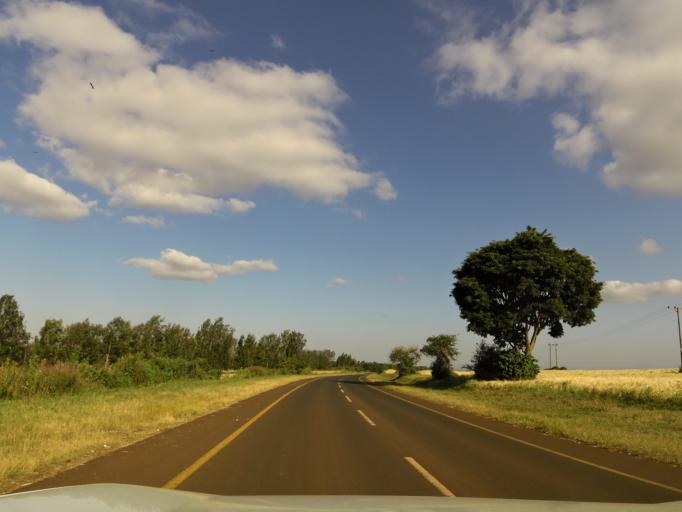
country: TZ
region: Arusha
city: Kiratu
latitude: -3.3180
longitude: 35.5973
